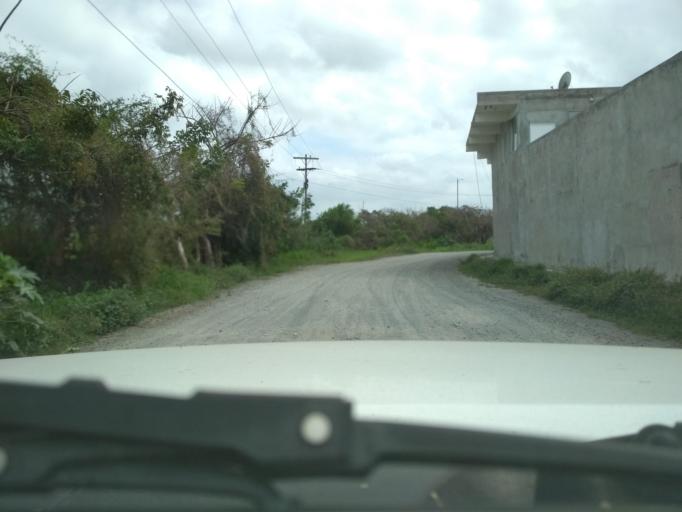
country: MX
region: Veracruz
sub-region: Veracruz
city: Fraccionamiento Geovillas los Pinos
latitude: 19.2423
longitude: -96.2560
